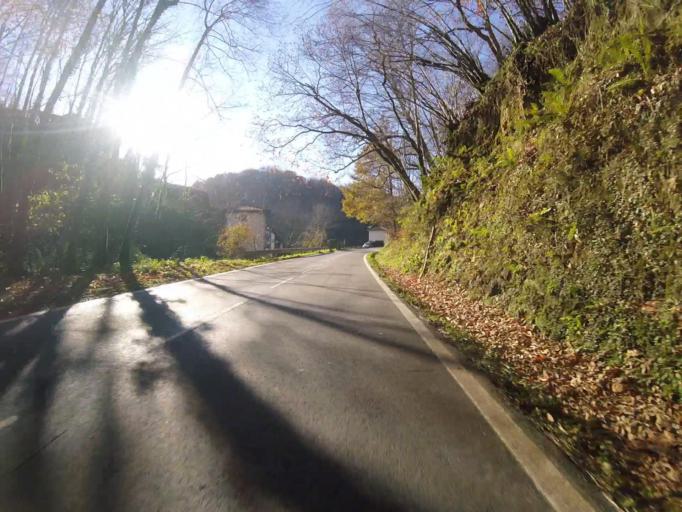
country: ES
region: Navarre
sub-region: Provincia de Navarra
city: Bera
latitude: 43.2817
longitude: -1.6525
